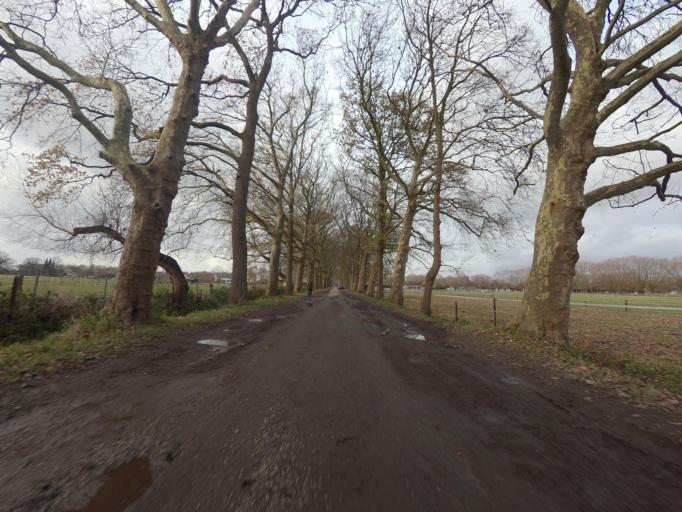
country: BE
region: Flanders
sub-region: Provincie Antwerpen
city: Hoboken
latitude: 51.1586
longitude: 4.3581
